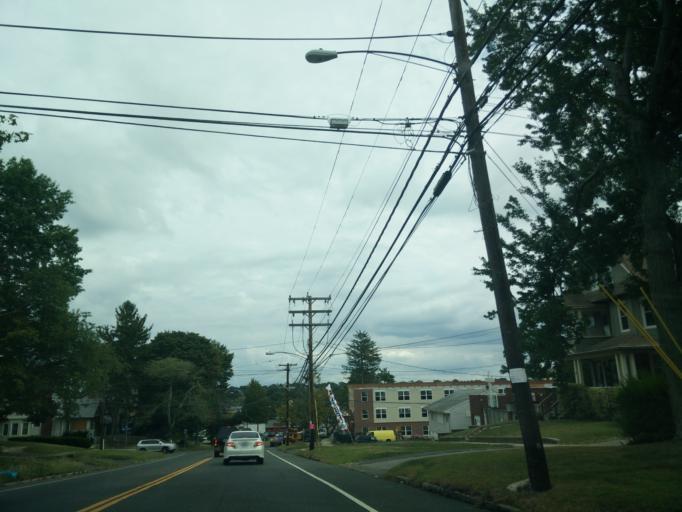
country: US
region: Connecticut
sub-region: Fairfield County
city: Stratford
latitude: 41.1935
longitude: -73.1627
